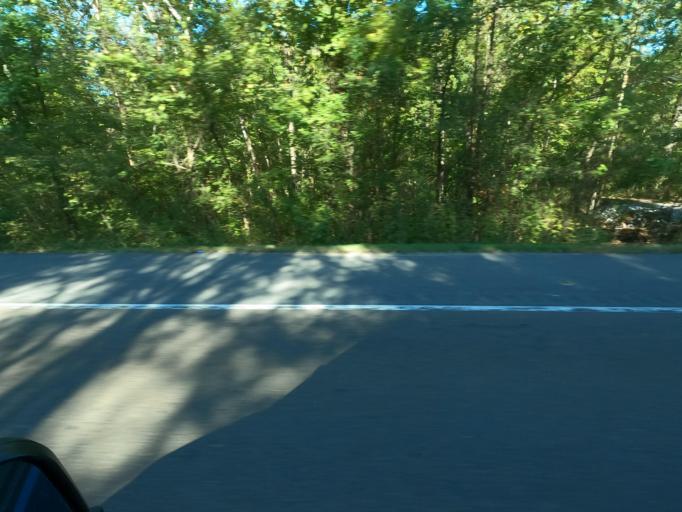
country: US
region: Tennessee
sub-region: Tipton County
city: Atoka
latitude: 35.4406
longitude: -89.7955
